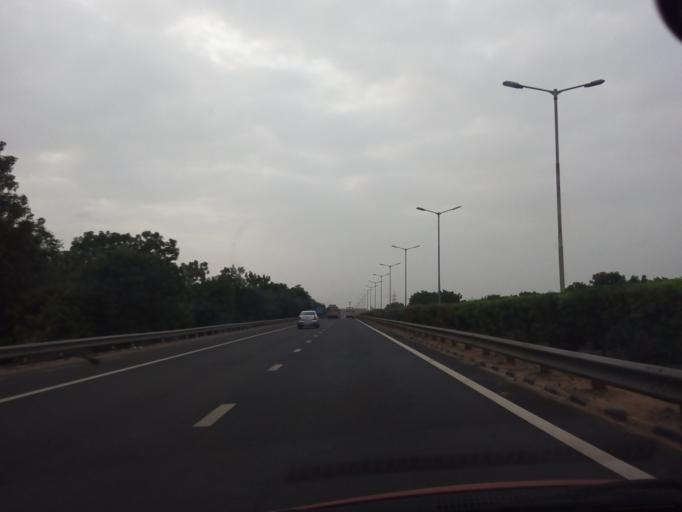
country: IN
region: Gujarat
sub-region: Ahmadabad
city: Ahmedabad
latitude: 22.9799
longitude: 72.6434
